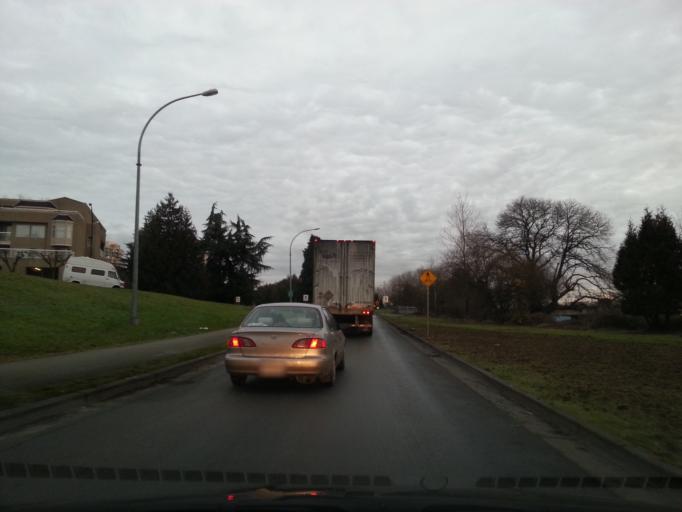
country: CA
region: British Columbia
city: New Westminster
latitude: 49.2083
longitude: -122.9006
